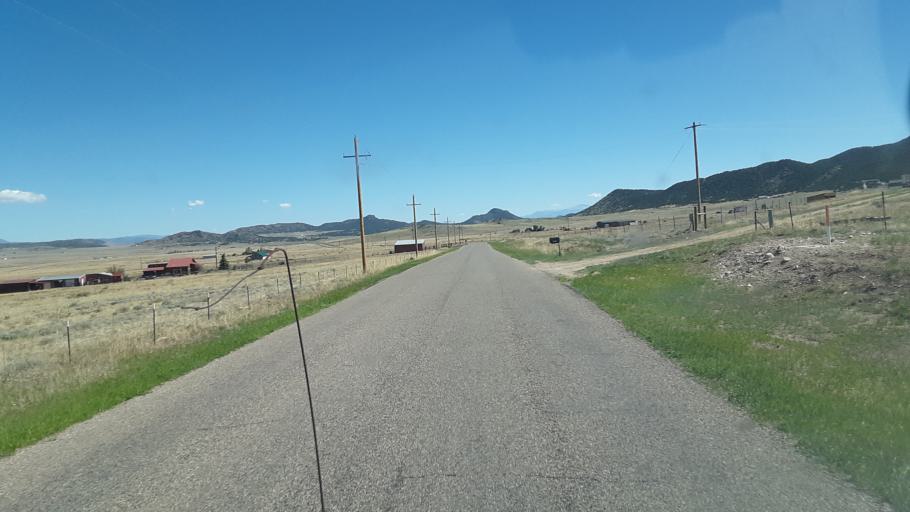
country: US
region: Colorado
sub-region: Custer County
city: Westcliffe
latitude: 38.1658
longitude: -105.4633
